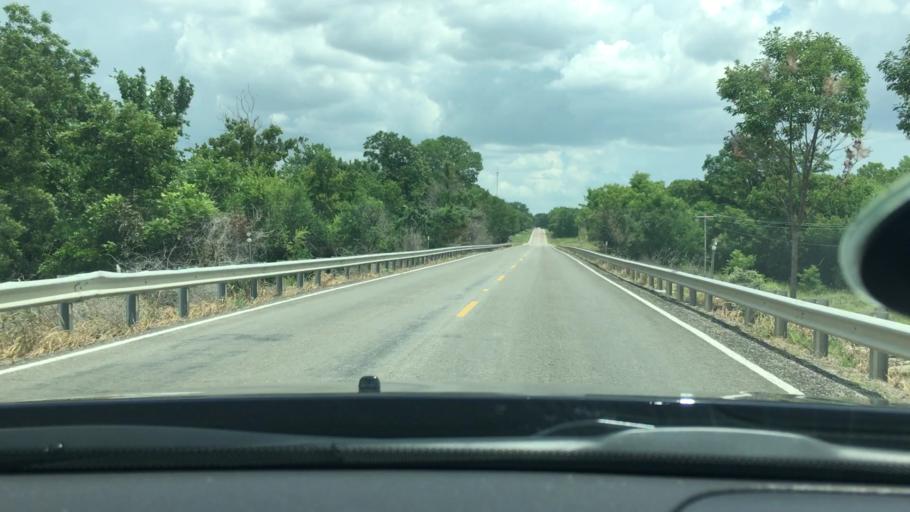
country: US
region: Texas
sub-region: Grayson County
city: Sherwood Shores
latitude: 33.9837
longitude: -96.8999
